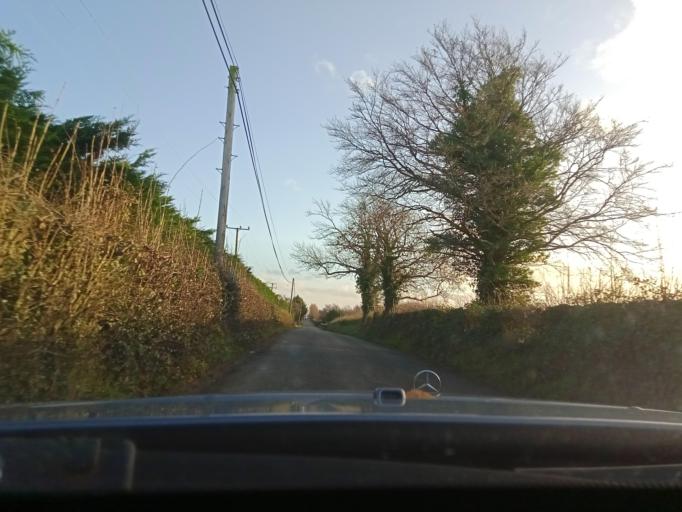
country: IE
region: Leinster
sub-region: Kilkenny
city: Callan
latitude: 52.5333
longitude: -7.3767
